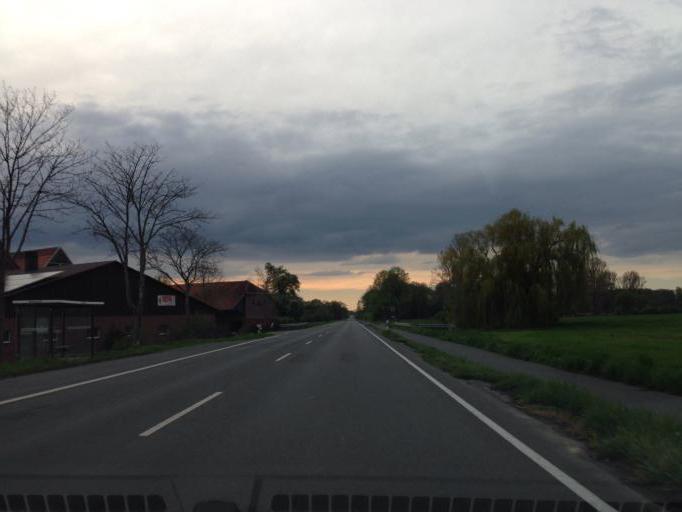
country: DE
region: North Rhine-Westphalia
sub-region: Regierungsbezirk Munster
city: Altenberge
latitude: 52.0104
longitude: 7.5280
